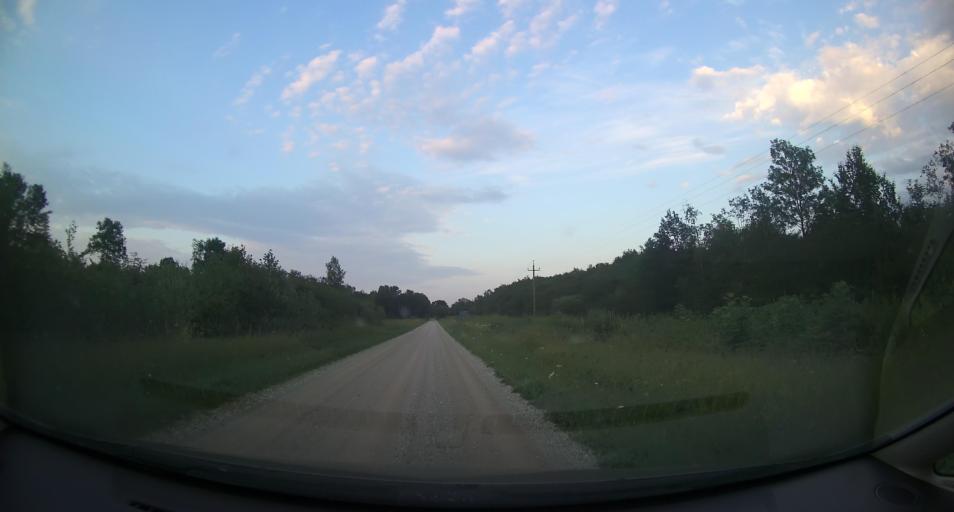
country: EE
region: Laeaene
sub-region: Lihula vald
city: Lihula
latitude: 58.5774
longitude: 23.6153
